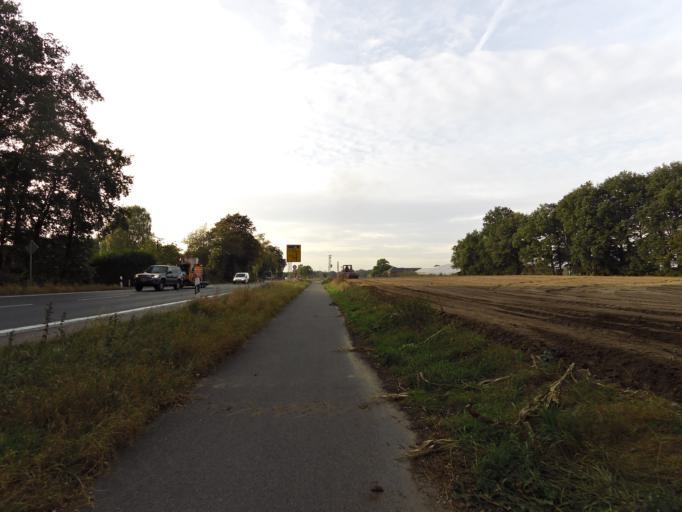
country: DE
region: North Rhine-Westphalia
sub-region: Regierungsbezirk Munster
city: Isselburg
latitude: 51.8126
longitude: 6.4813
